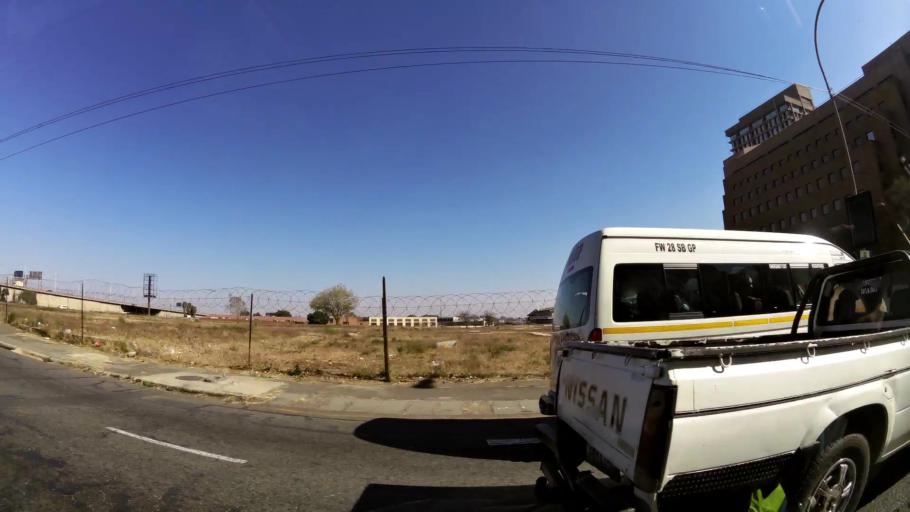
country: ZA
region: Gauteng
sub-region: City of Johannesburg Metropolitan Municipality
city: Johannesburg
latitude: -26.2101
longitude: 28.0386
